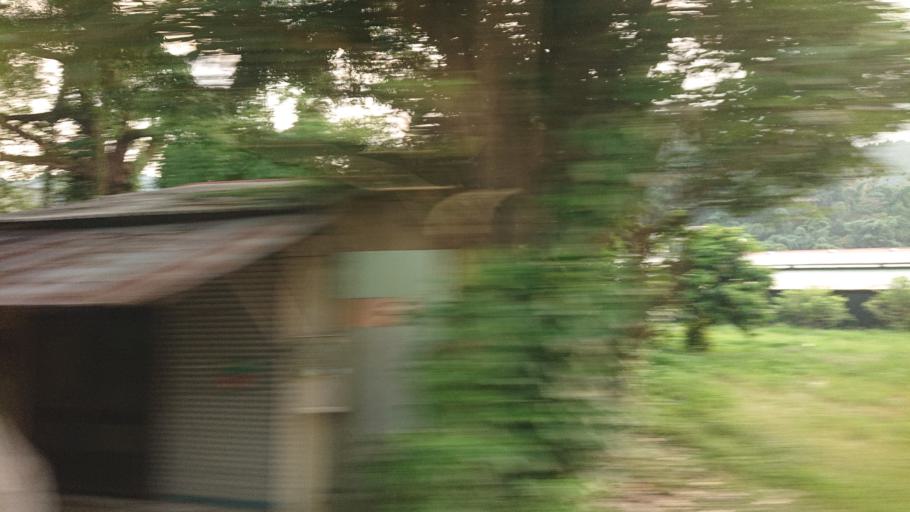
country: TW
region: Taiwan
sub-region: Nantou
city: Puli
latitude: 23.9668
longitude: 120.9994
